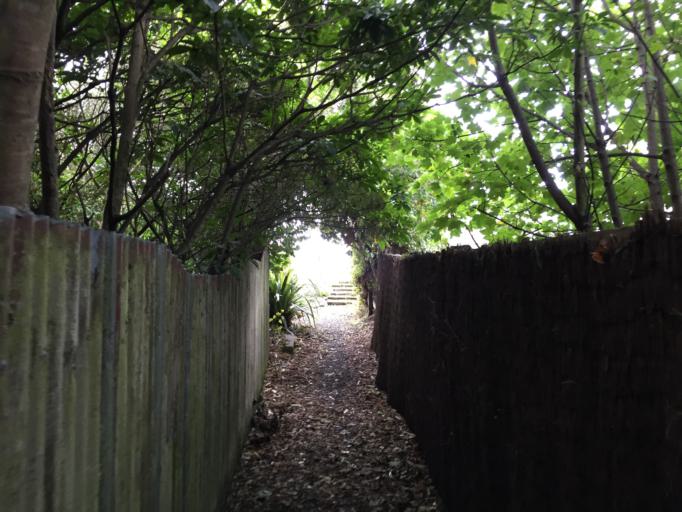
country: NZ
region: Southland
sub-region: Southland District
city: Riverton
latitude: -46.3720
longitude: 168.0275
